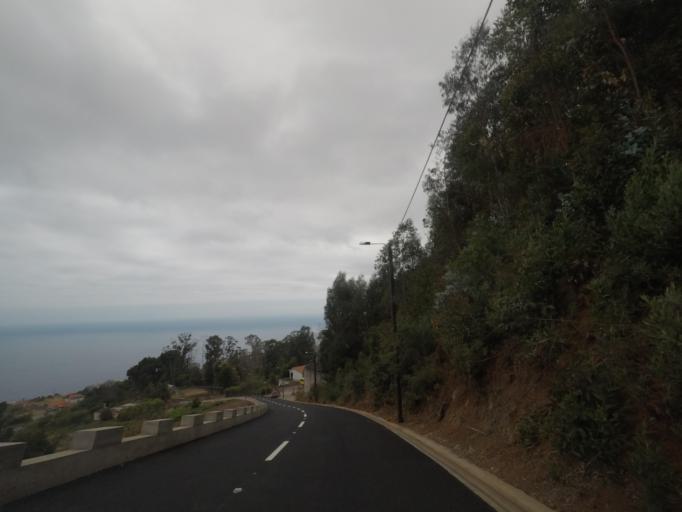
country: PT
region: Madeira
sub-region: Calheta
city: Estreito da Calheta
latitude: 32.7414
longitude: -17.1630
